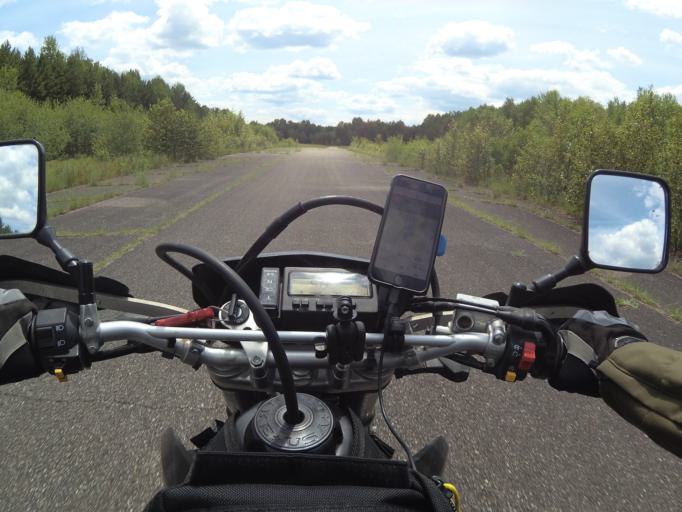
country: CA
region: Ontario
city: Bancroft
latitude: 45.0296
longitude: -77.2656
